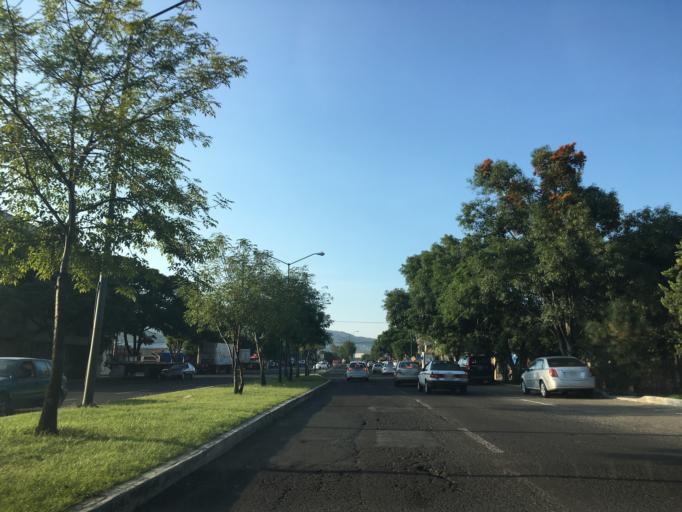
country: MX
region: Michoacan
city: Morelia
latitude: 19.7056
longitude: -101.2252
